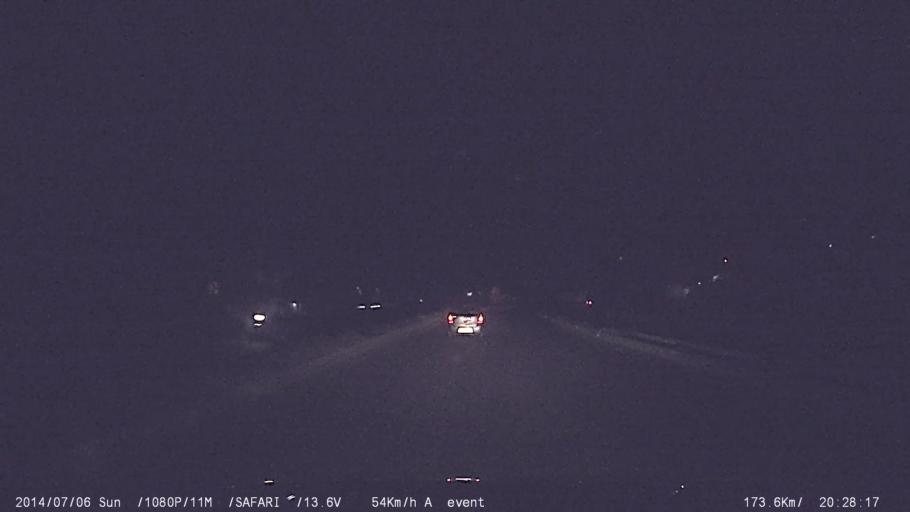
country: IN
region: Kerala
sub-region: Palakkad district
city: Chittur
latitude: 10.7993
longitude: 76.7587
